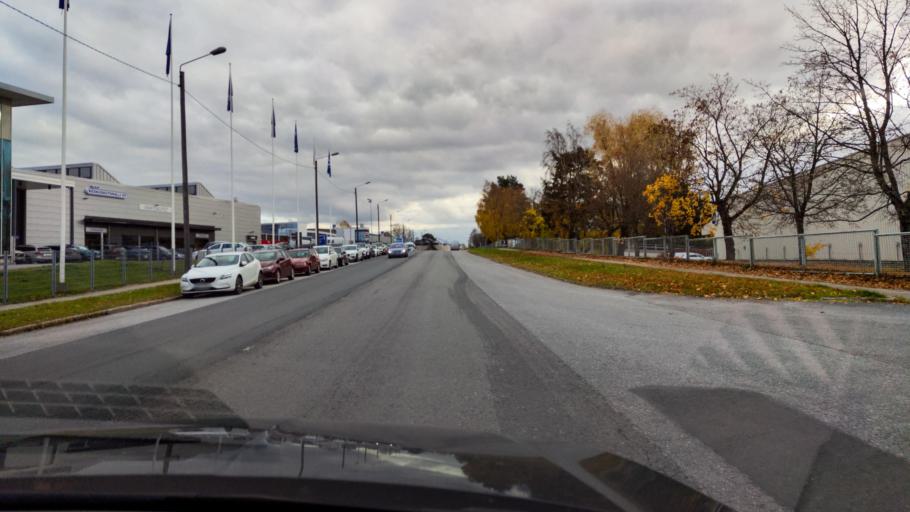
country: FI
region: Varsinais-Suomi
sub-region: Turku
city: Turku
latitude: 60.4725
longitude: 22.2616
